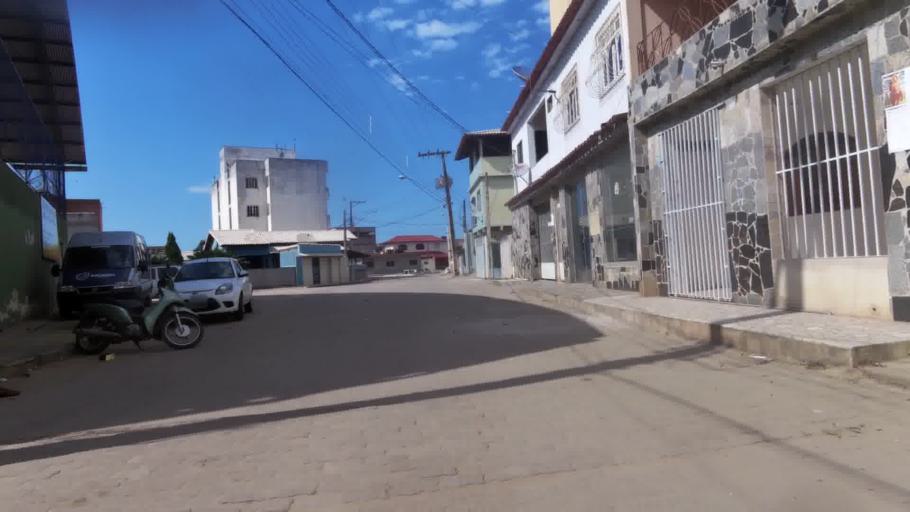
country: BR
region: Espirito Santo
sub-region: Piuma
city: Piuma
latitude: -20.8507
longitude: -40.7530
